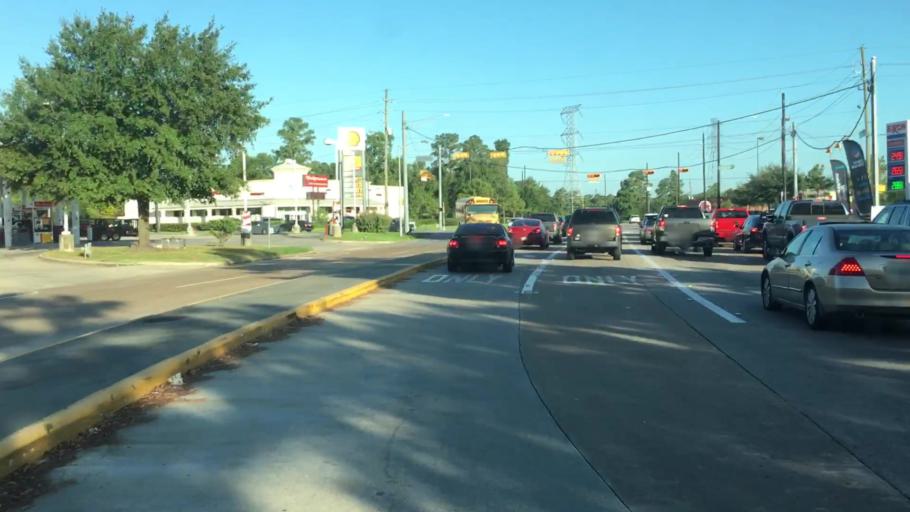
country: US
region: Texas
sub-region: Harris County
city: Atascocita
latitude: 29.9788
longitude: -95.2169
